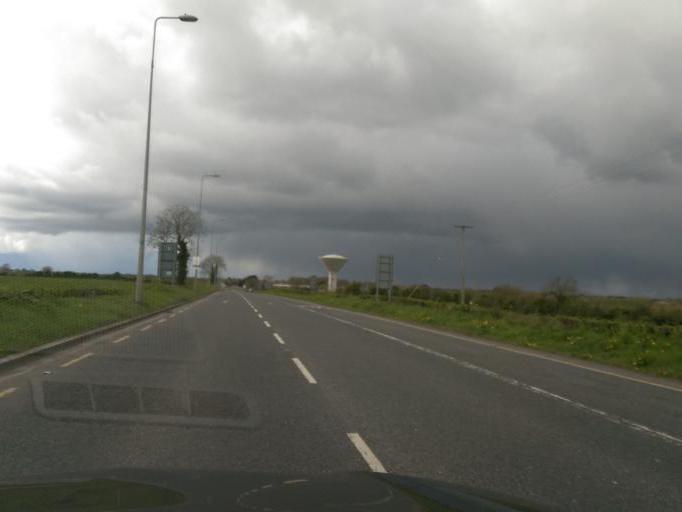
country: IE
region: Leinster
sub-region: An Mhi
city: Dunshaughlin
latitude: 53.5181
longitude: -6.5463
